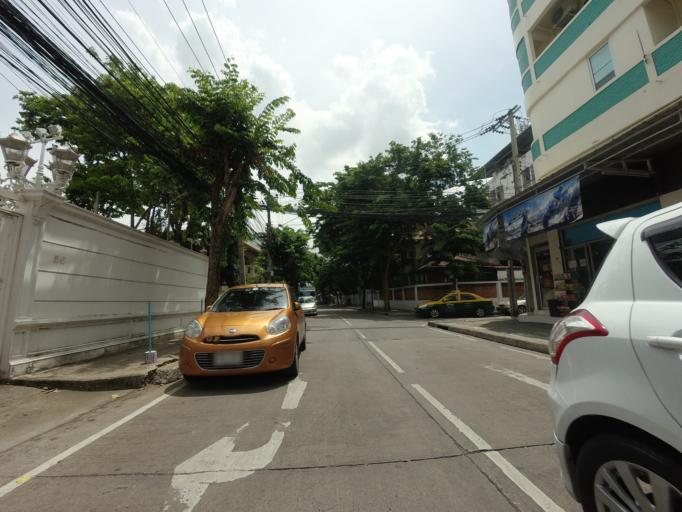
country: TH
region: Bangkok
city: Din Daeng
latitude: 13.7767
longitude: 100.5588
